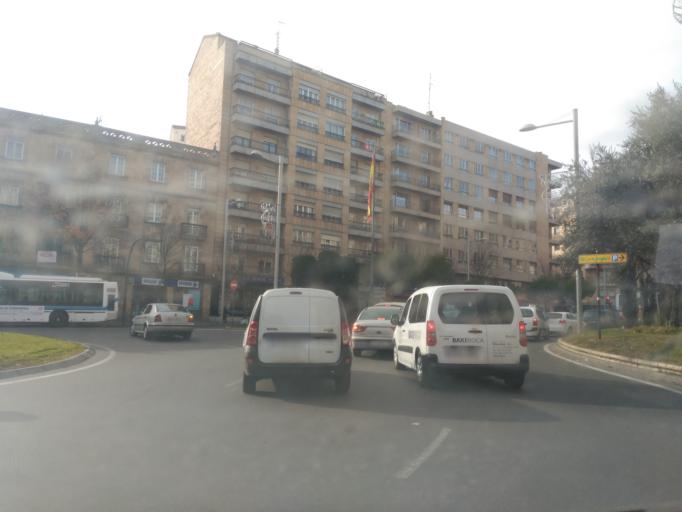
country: ES
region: Castille and Leon
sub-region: Provincia de Salamanca
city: Salamanca
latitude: 40.9686
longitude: -5.6585
